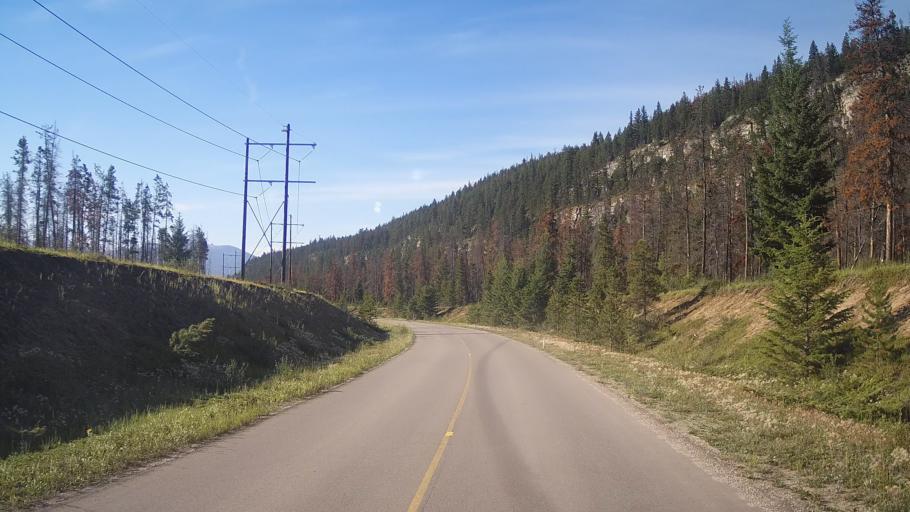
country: CA
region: Alberta
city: Jasper Park Lodge
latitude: 52.9903
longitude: -118.0832
